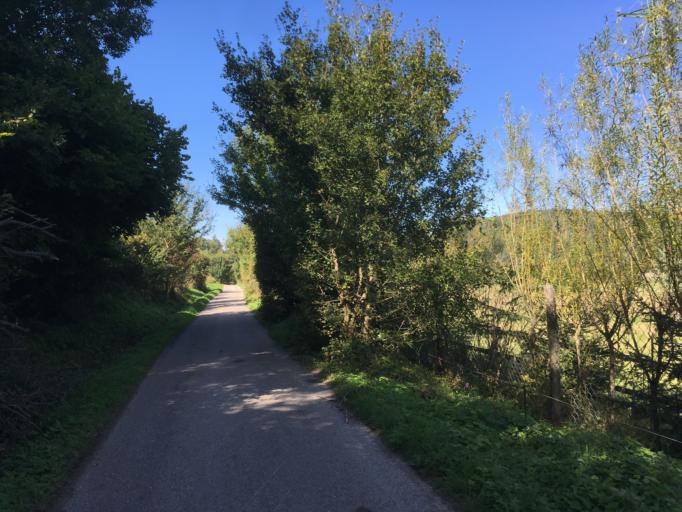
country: SK
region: Trenciansky
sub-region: Okres Povazska Bystrica
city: Povazska Bystrica
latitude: 49.0314
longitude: 18.4339
